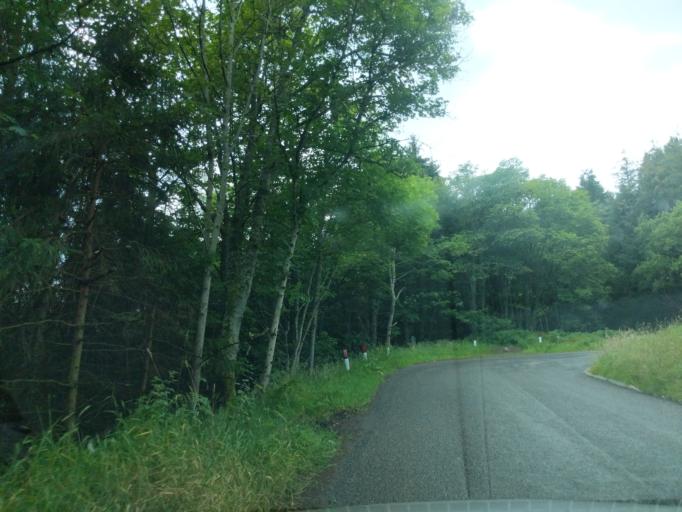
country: GB
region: Scotland
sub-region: Moray
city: Rothes
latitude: 57.4582
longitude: -3.3018
